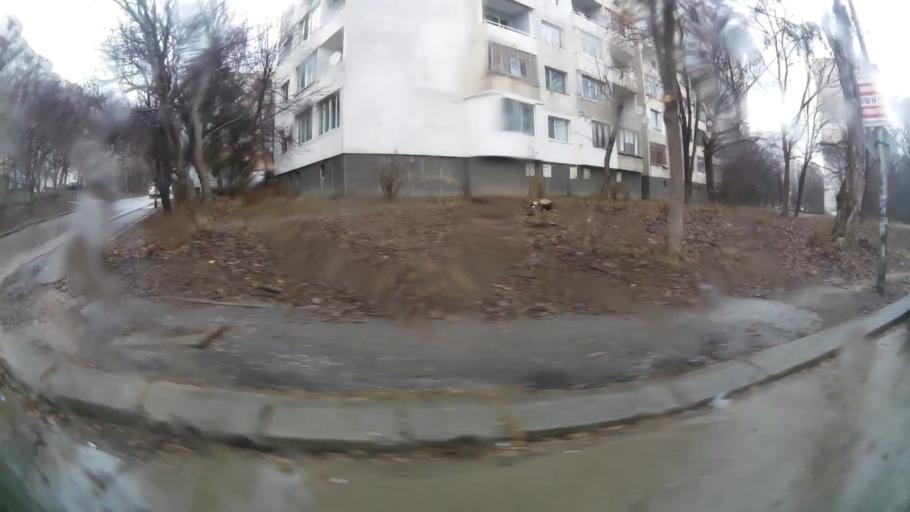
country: BG
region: Sofia-Capital
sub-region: Stolichna Obshtina
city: Sofia
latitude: 42.6513
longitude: 23.3651
